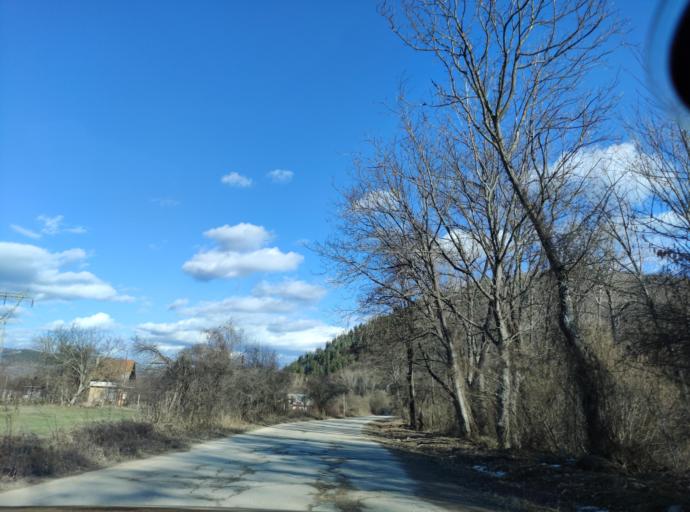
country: BG
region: Montana
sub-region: Obshtina Chiprovtsi
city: Chiprovtsi
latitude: 43.4164
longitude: 22.9476
